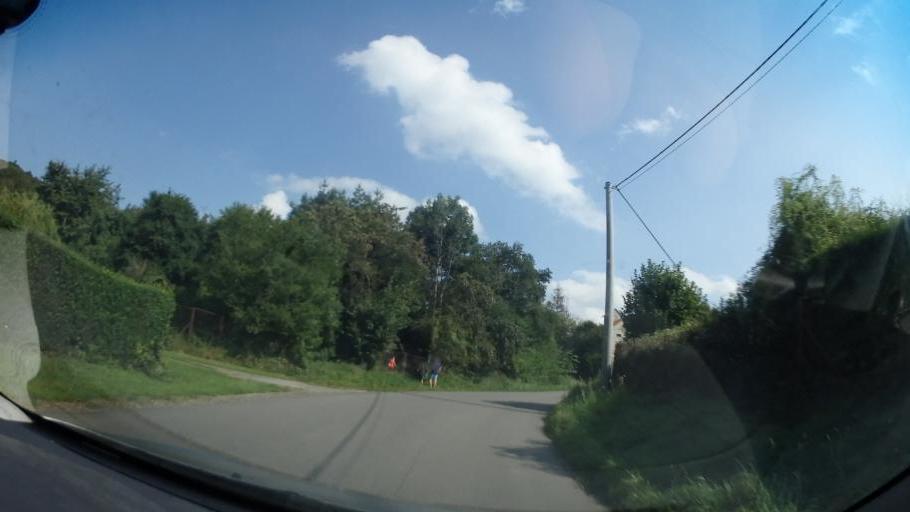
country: CZ
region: South Moravian
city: Olesnice
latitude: 49.5421
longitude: 16.3607
